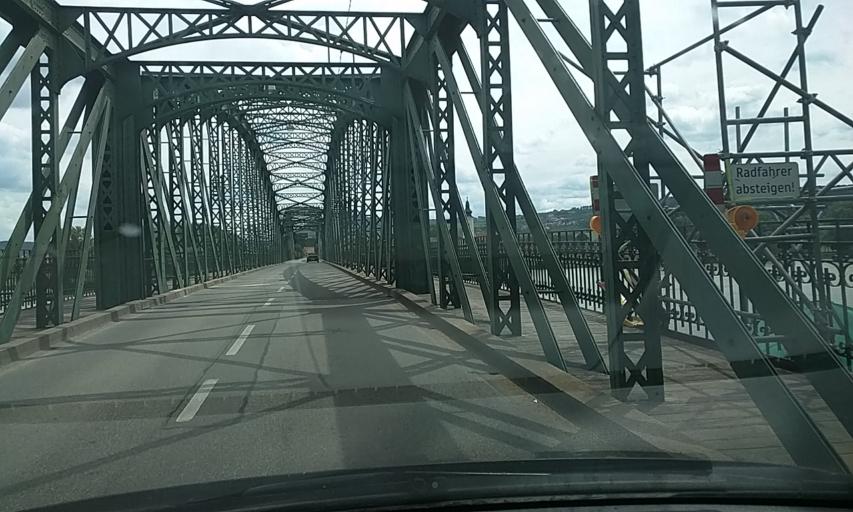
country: AT
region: Lower Austria
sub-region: Politischer Bezirk Krems
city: Weinzierl bei Krems
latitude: 48.3993
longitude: 15.5740
